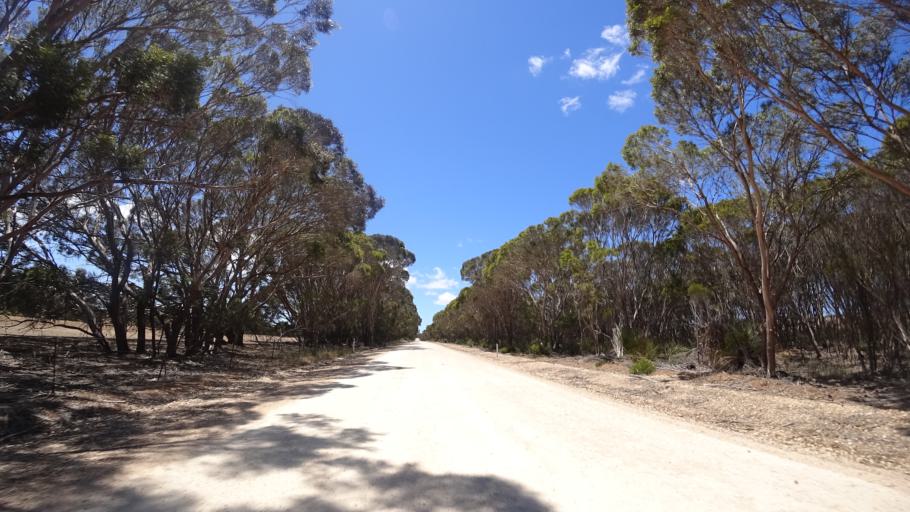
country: AU
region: South Australia
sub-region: Kangaroo Island
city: Kingscote
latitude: -35.8270
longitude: 137.9815
